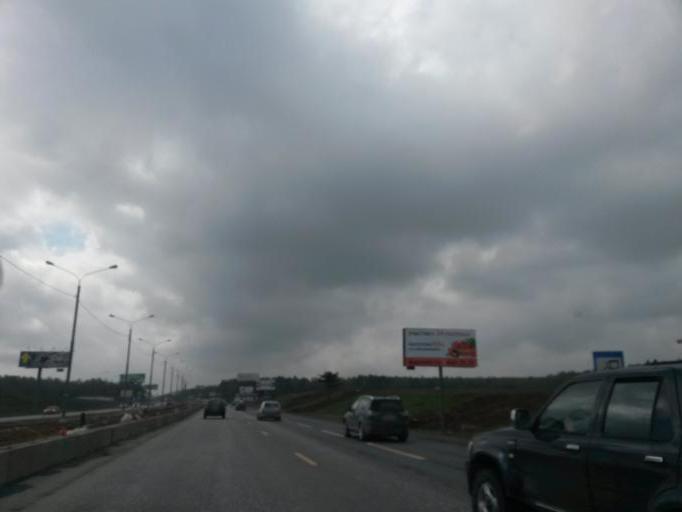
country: RU
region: Moskovskaya
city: Shcherbinka
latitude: 55.5249
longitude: 37.6096
